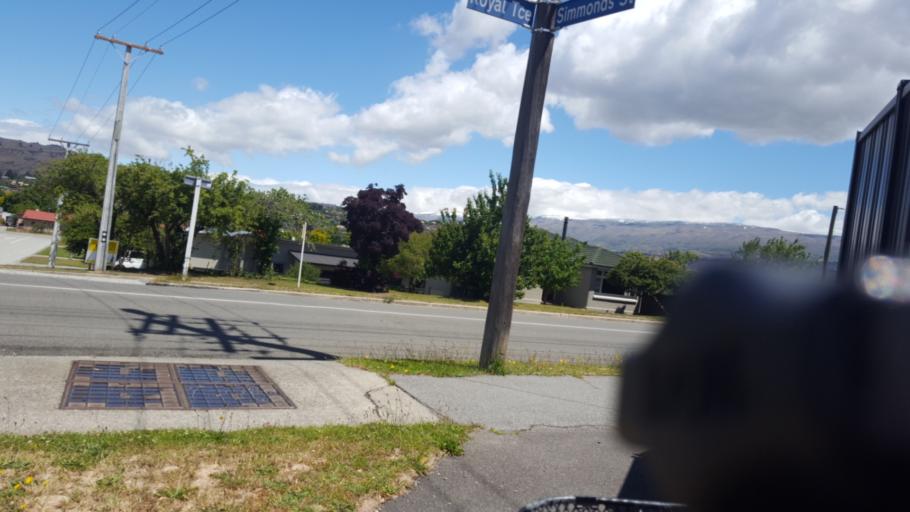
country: NZ
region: Otago
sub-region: Queenstown-Lakes District
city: Wanaka
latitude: -45.2473
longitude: 169.3908
